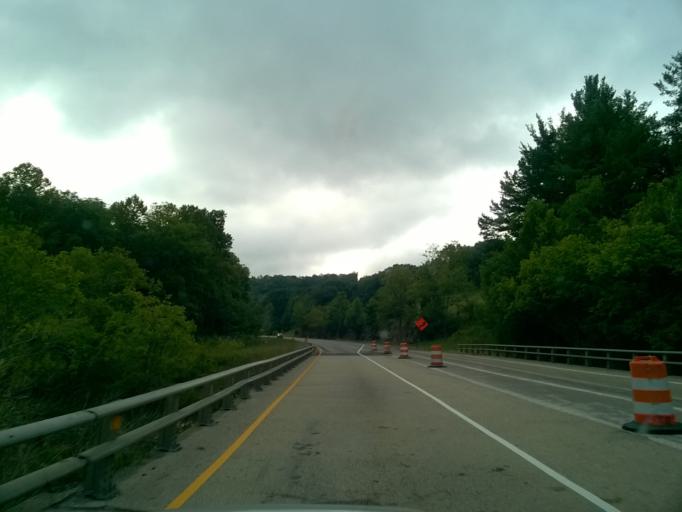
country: US
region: Indiana
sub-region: Crawford County
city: English
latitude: 38.2383
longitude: -86.4054
